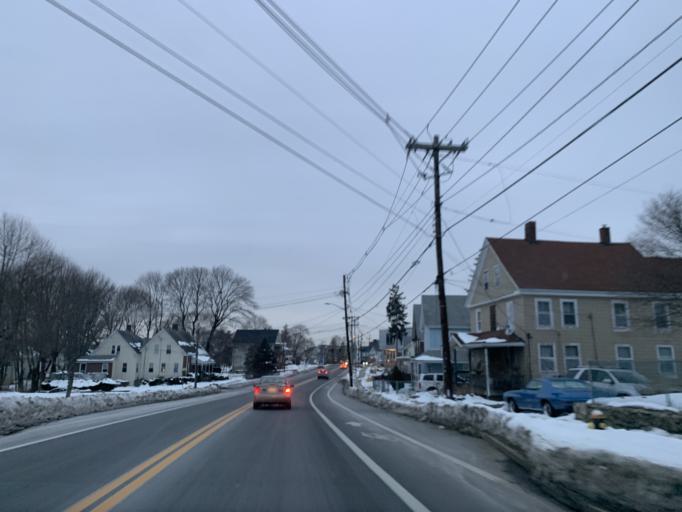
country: US
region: Massachusetts
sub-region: Norfolk County
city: Stoughton
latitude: 42.1218
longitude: -71.0971
